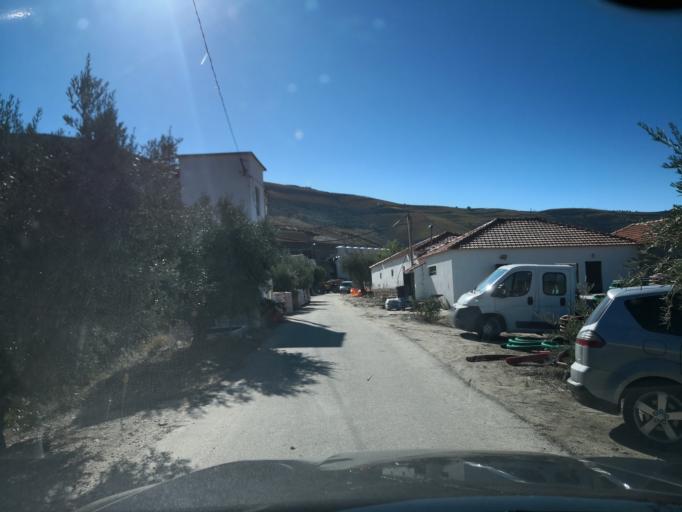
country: PT
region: Viseu
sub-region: Tabuaco
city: Tabuaco
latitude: 41.1781
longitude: -7.5139
